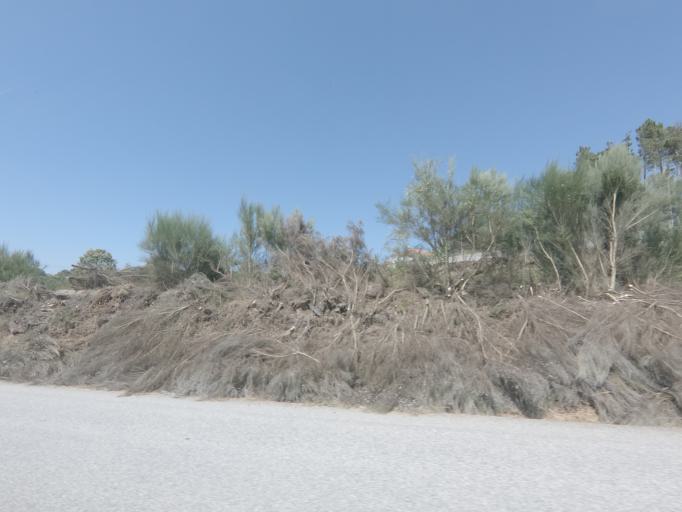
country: PT
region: Viseu
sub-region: Tarouca
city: Tarouca
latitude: 40.9904
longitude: -7.8127
